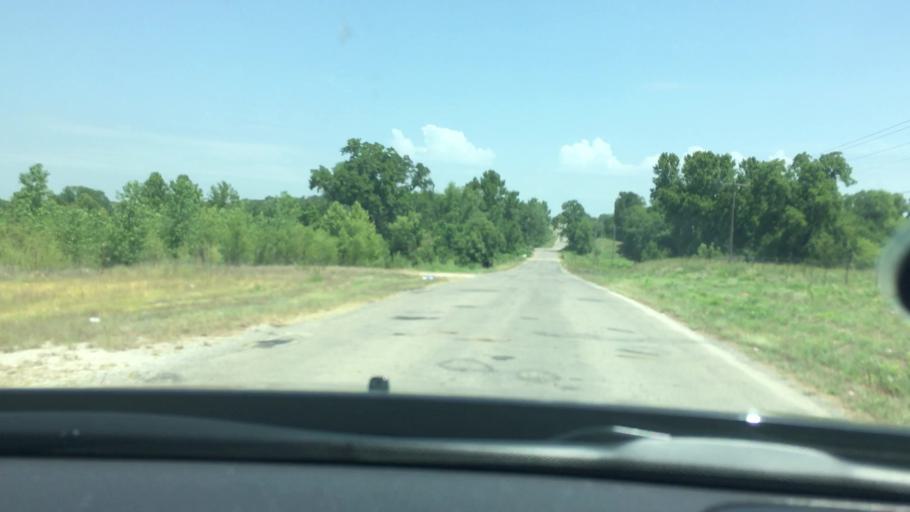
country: US
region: Oklahoma
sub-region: Pontotoc County
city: Byng
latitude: 34.8377
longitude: -96.6698
